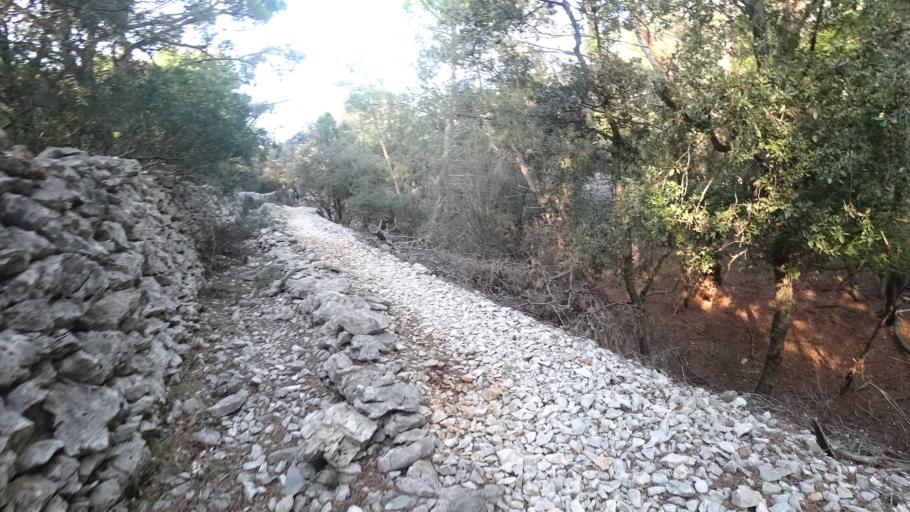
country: HR
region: Primorsko-Goranska
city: Mali Losinj
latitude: 44.5152
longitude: 14.4765
